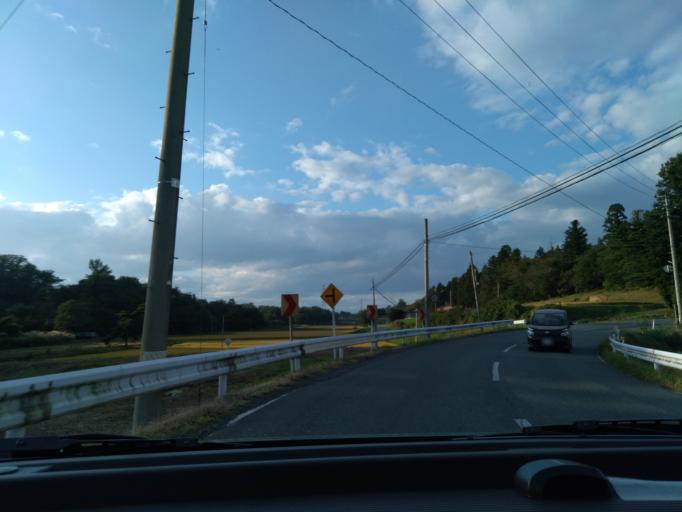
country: JP
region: Iwate
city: Ichinoseki
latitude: 38.8728
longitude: 141.1956
